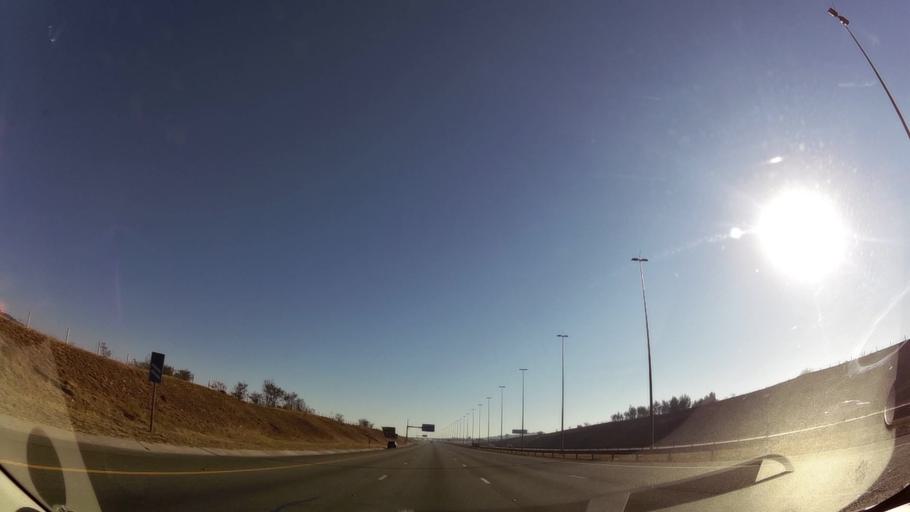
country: ZA
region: Gauteng
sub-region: City of Tshwane Metropolitan Municipality
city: Centurion
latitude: -25.8753
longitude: 28.2545
